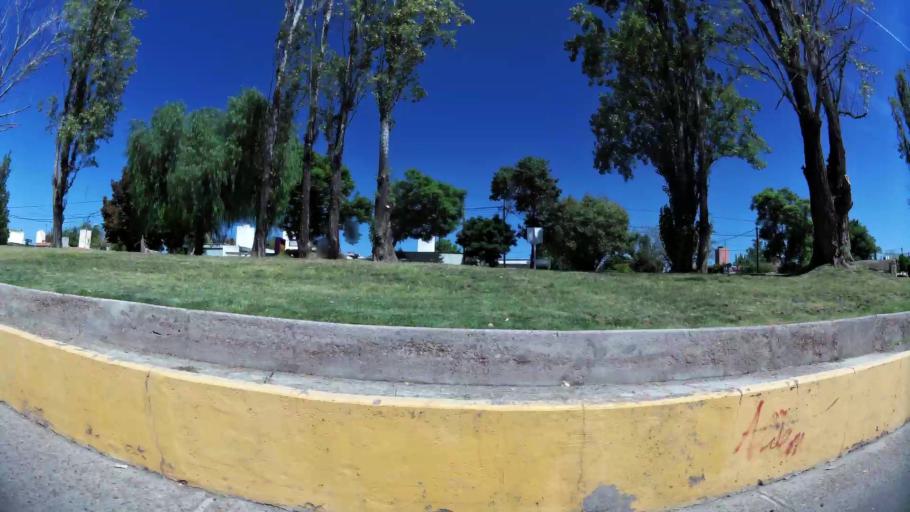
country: AR
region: Mendoza
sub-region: Departamento de Godoy Cruz
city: Godoy Cruz
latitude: -32.9465
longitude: -68.8565
